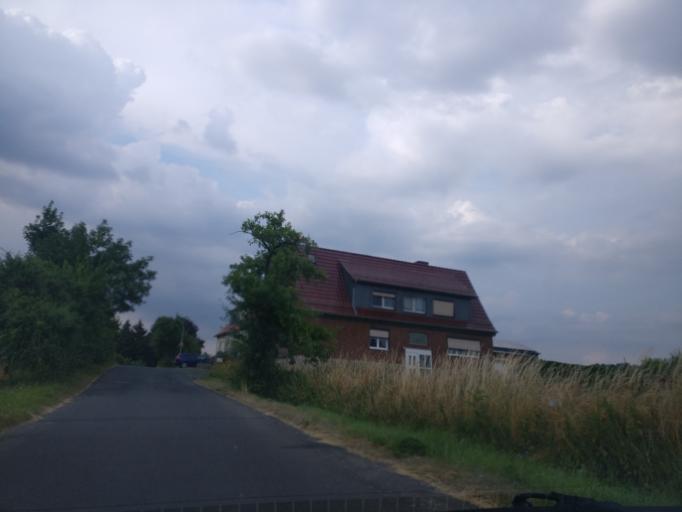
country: DE
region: Lower Saxony
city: Adelebsen
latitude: 51.5921
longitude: 9.7813
